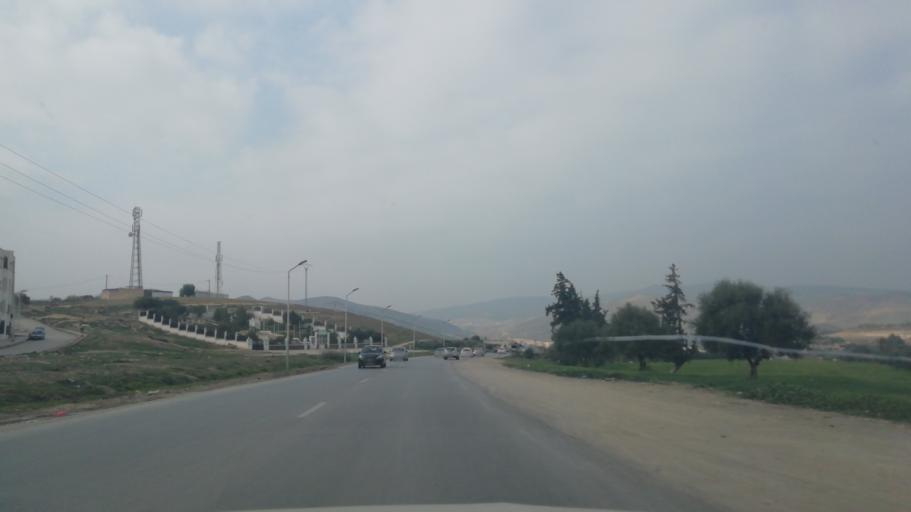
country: DZ
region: Mascara
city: Mascara
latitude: 35.4560
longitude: 0.0040
